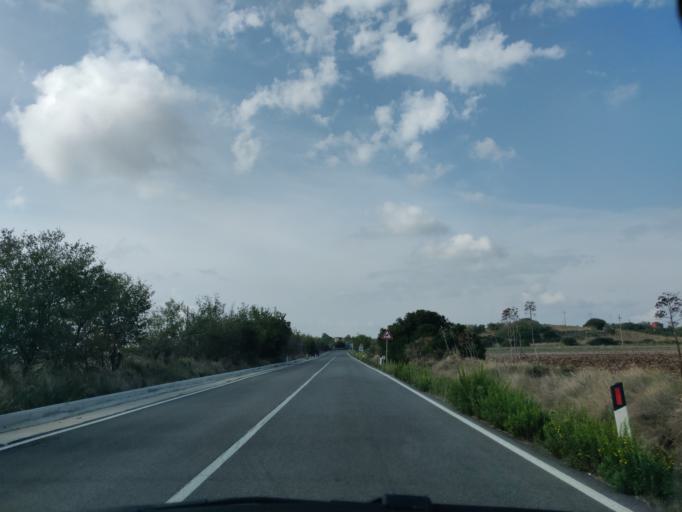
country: IT
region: Latium
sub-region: Provincia di Viterbo
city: Tarquinia
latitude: 42.2323
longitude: 11.7953
